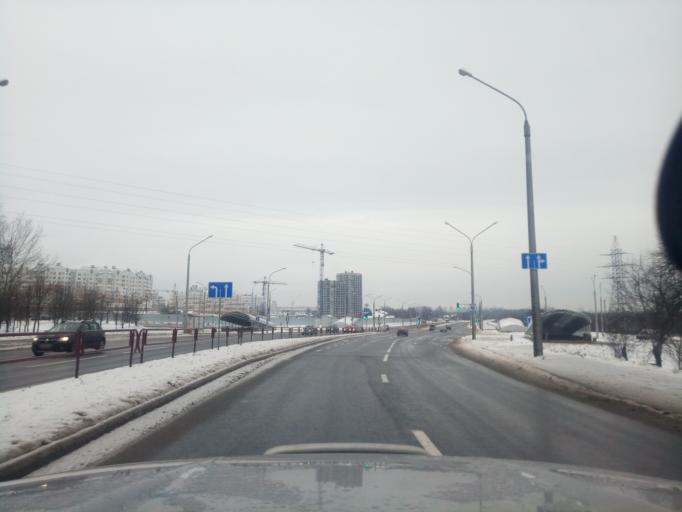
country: BY
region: Minsk
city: Machulishchy
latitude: 53.8362
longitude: 27.6002
